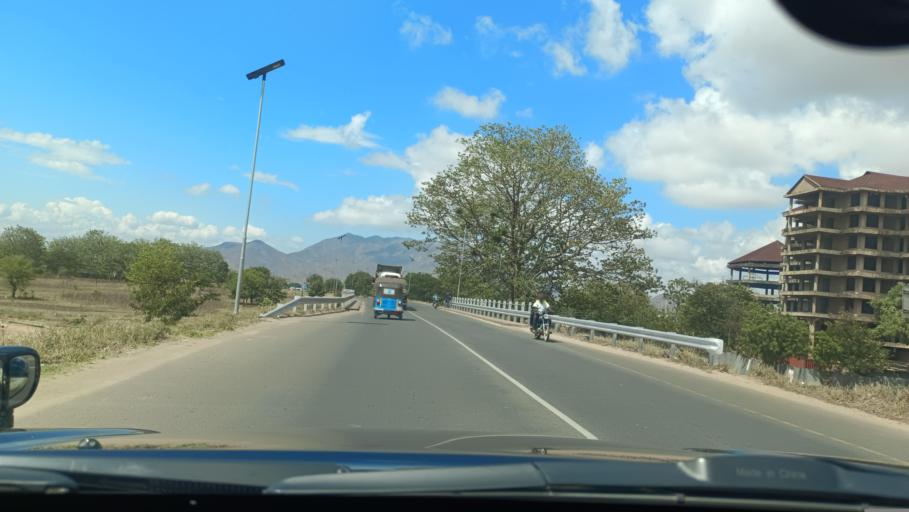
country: TZ
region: Morogoro
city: Morogoro
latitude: -6.8064
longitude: 37.6569
